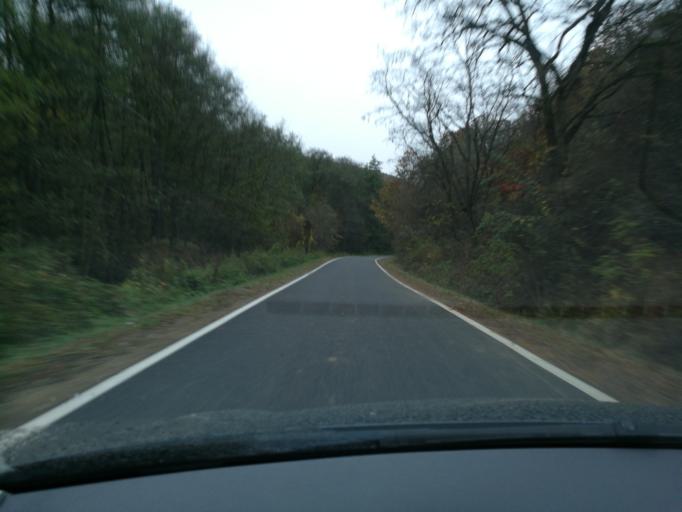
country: HU
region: Nograd
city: Paszto
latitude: 47.9707
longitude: 19.6232
